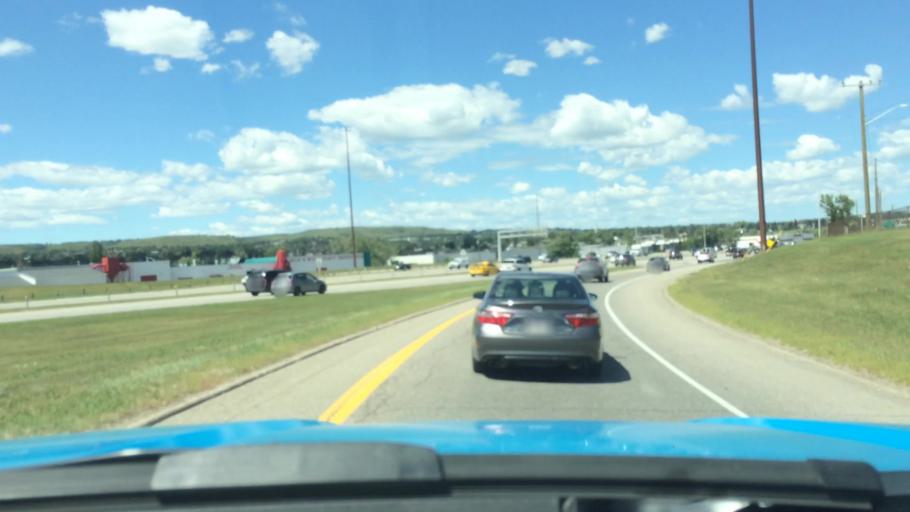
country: CA
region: Alberta
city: Calgary
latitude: 51.0986
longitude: -114.0414
